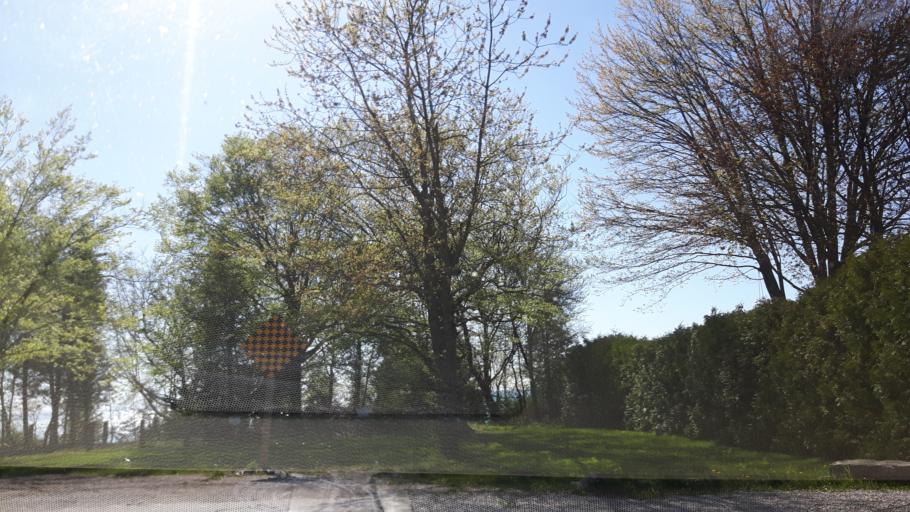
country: CA
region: Ontario
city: Bluewater
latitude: 43.5111
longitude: -81.7106
